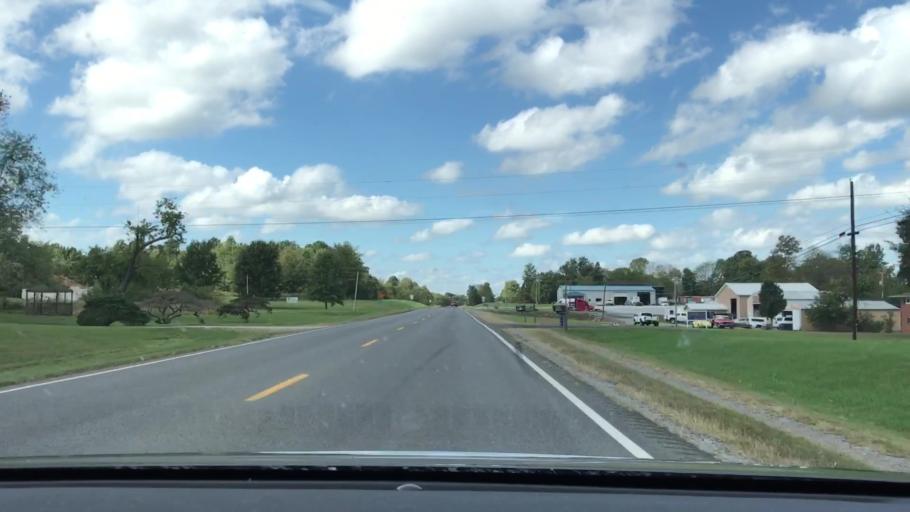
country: US
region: Kentucky
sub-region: McCracken County
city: Reidland
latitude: 37.0079
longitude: -88.4908
